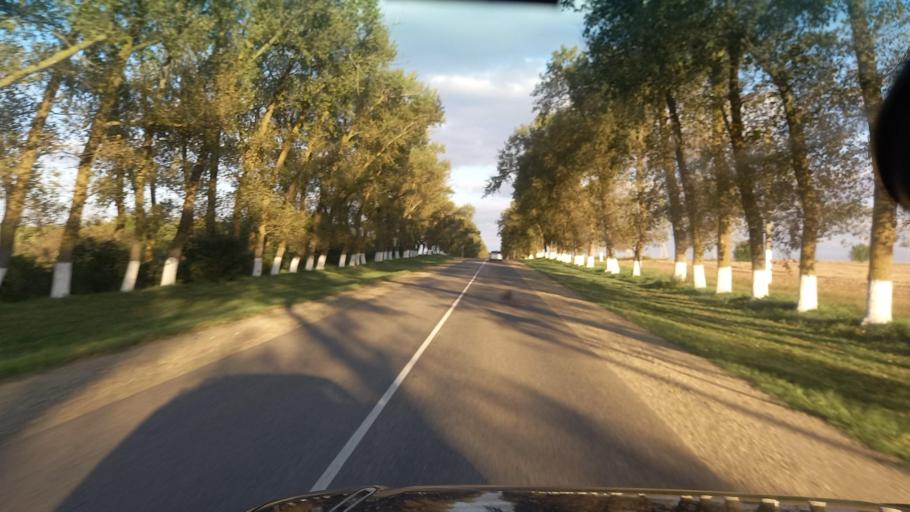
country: RU
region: Krasnodarskiy
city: Krymsk
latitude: 44.9399
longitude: 37.9304
